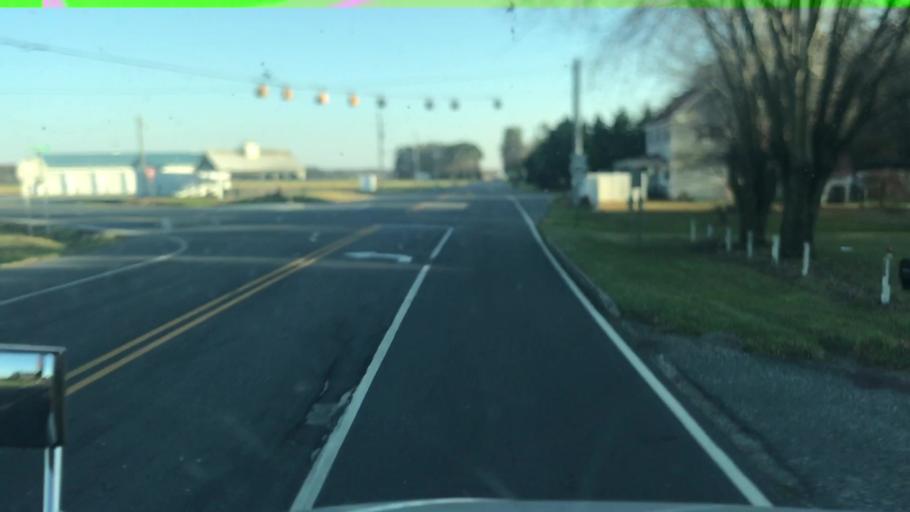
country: US
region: Delaware
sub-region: Sussex County
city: Bridgeville
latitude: 38.7809
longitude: -75.6679
